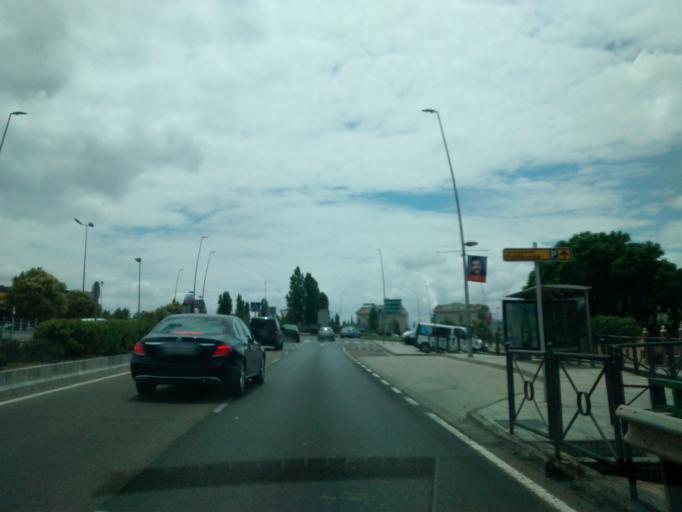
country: ES
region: Extremadura
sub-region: Provincia de Badajoz
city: Merida
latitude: 38.9174
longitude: -6.3303
